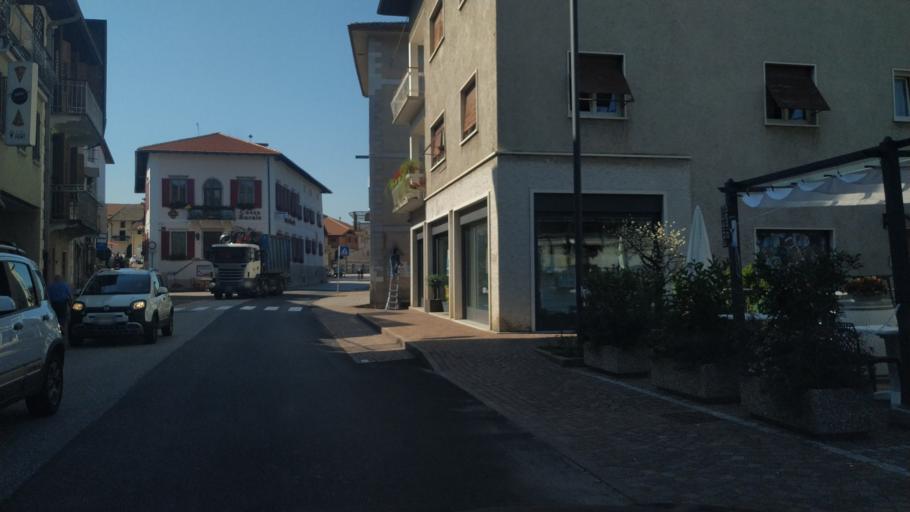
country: IT
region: Trentino-Alto Adige
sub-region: Provincia di Trento
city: Cavareno
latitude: 46.4099
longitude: 11.1376
